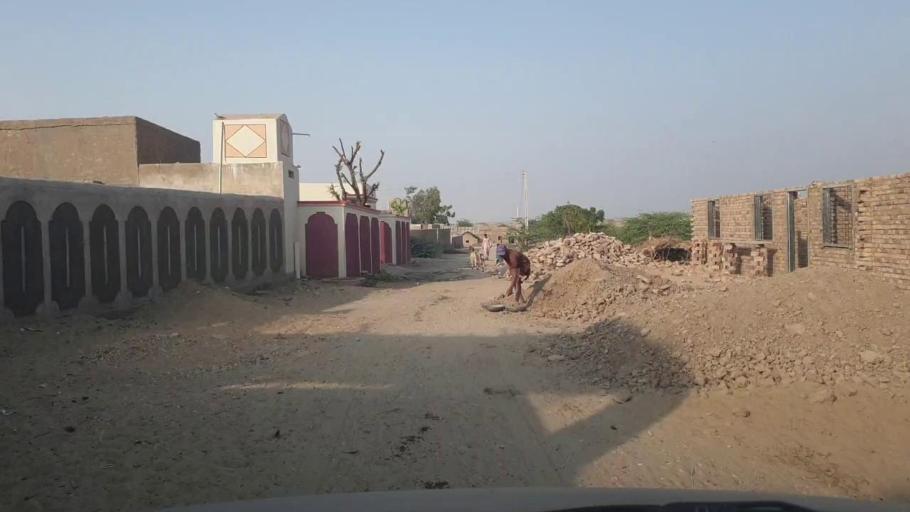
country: PK
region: Sindh
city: Umarkot
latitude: 25.3495
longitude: 69.7648
